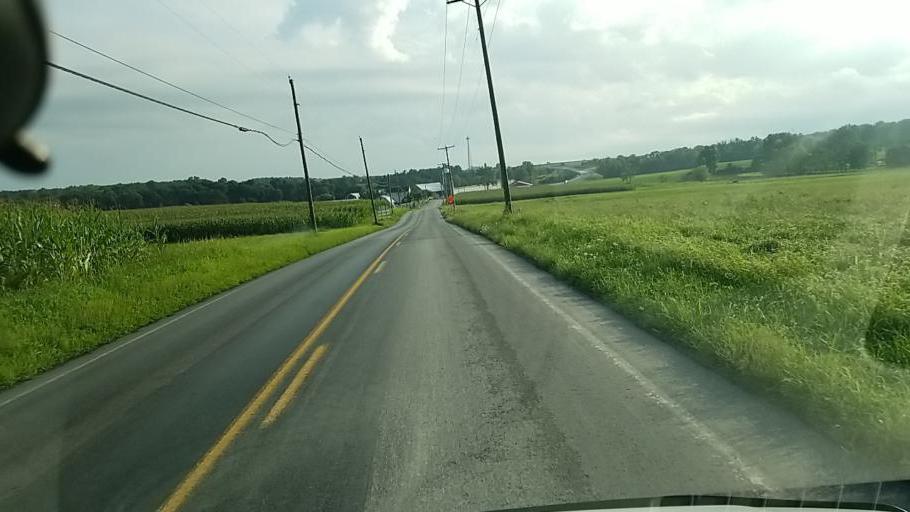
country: US
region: Pennsylvania
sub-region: Cumberland County
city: Shippensburg
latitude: 40.1799
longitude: -77.5362
